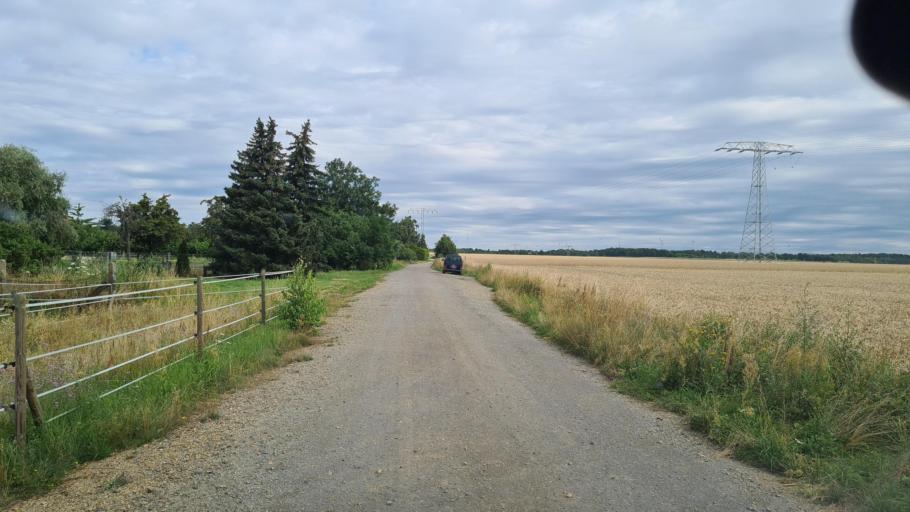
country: DE
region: Brandenburg
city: Grossraschen
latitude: 51.5509
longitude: 14.0636
